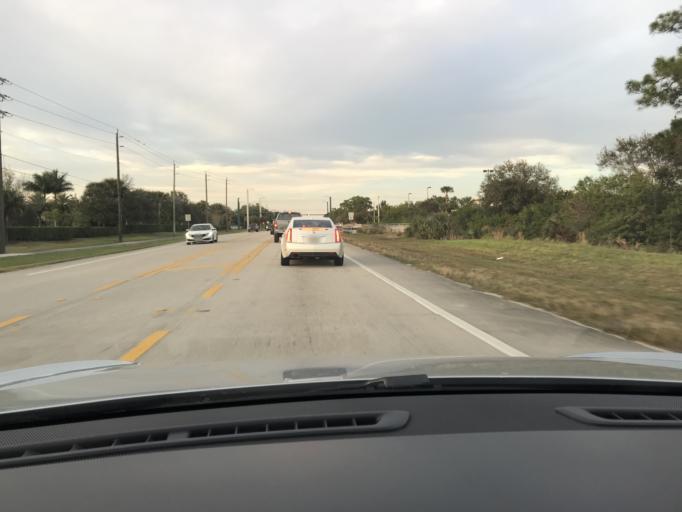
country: US
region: Florida
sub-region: Indian River County
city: Vero Beach South
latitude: 27.5852
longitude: -80.4307
